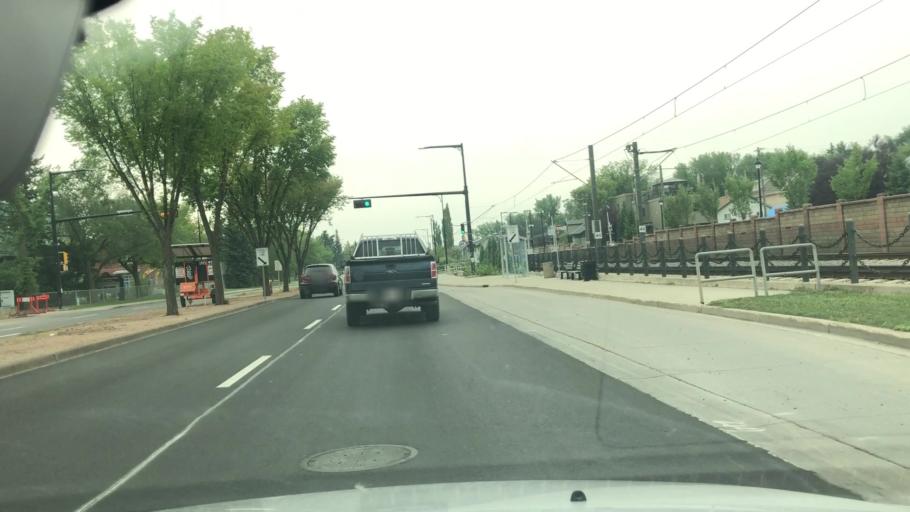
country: CA
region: Alberta
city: Edmonton
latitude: 53.5146
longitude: -113.5260
